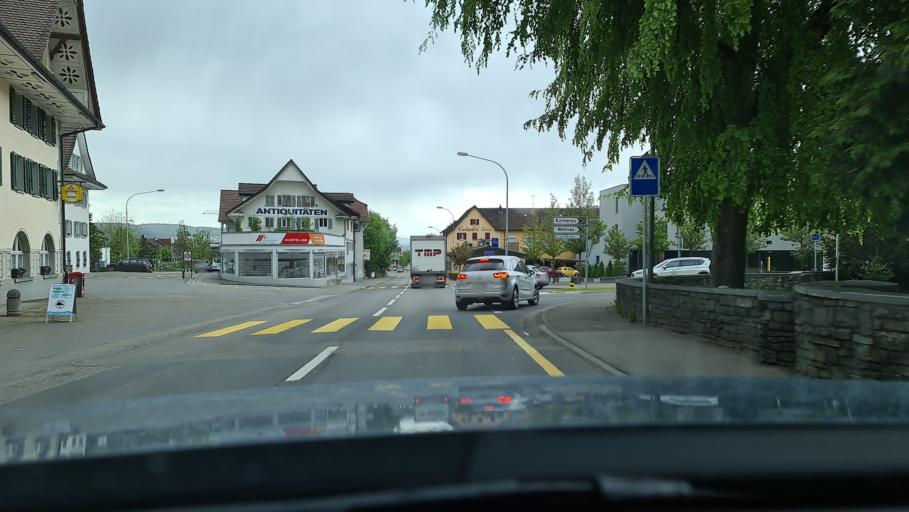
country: CH
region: Lucerne
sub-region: Sursee District
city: Triengen
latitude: 47.2350
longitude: 8.0764
